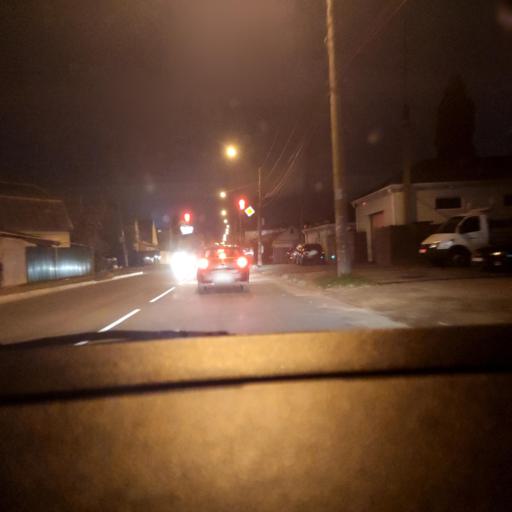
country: RU
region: Voronezj
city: Voronezh
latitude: 51.6886
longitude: 39.2101
